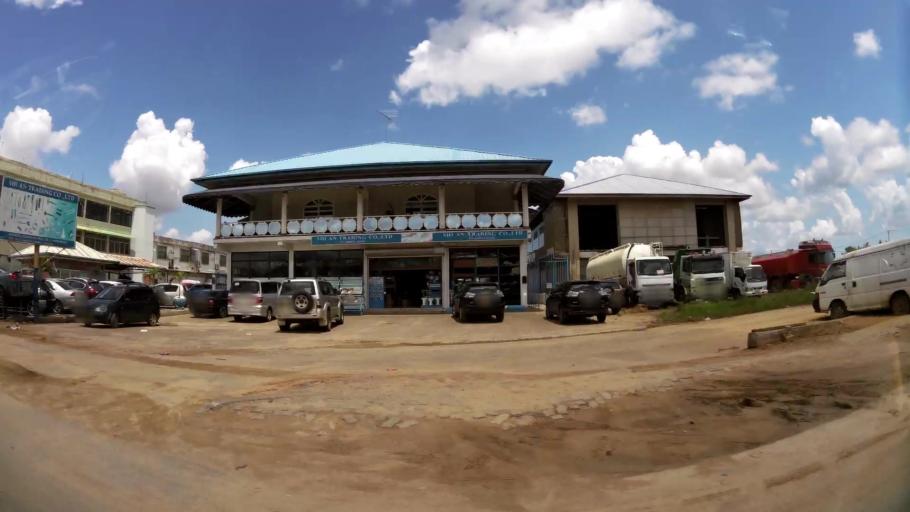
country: SR
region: Paramaribo
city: Paramaribo
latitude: 5.8110
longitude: -55.1537
